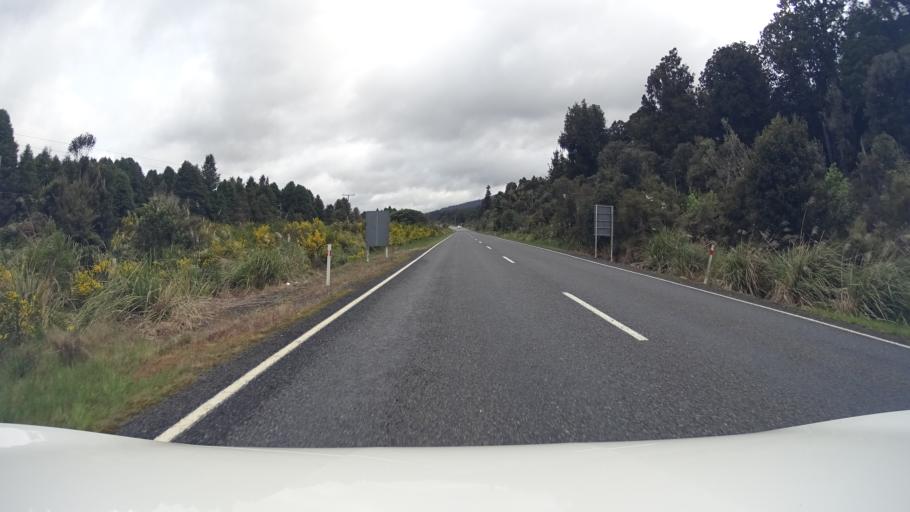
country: NZ
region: Manawatu-Wanganui
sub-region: Ruapehu District
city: Waiouru
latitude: -39.2458
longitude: 175.3897
